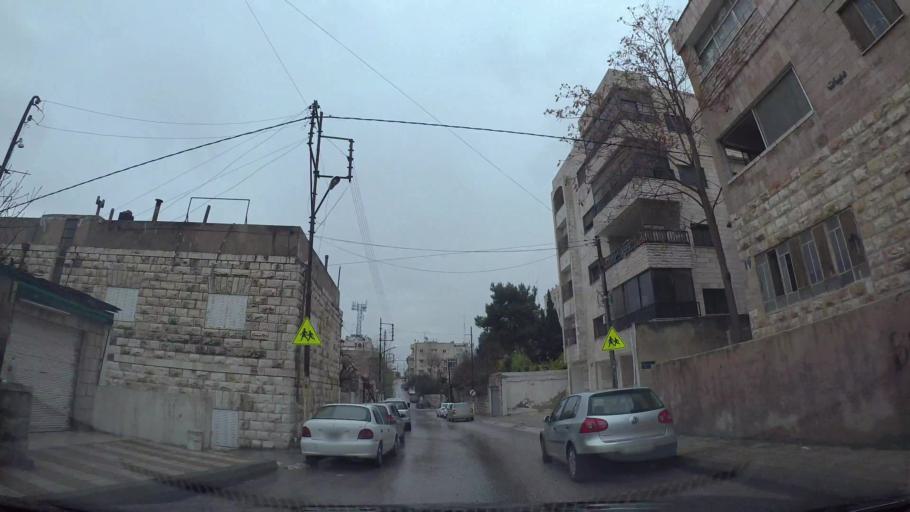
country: JO
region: Amman
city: Amman
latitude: 31.9579
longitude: 35.9248
